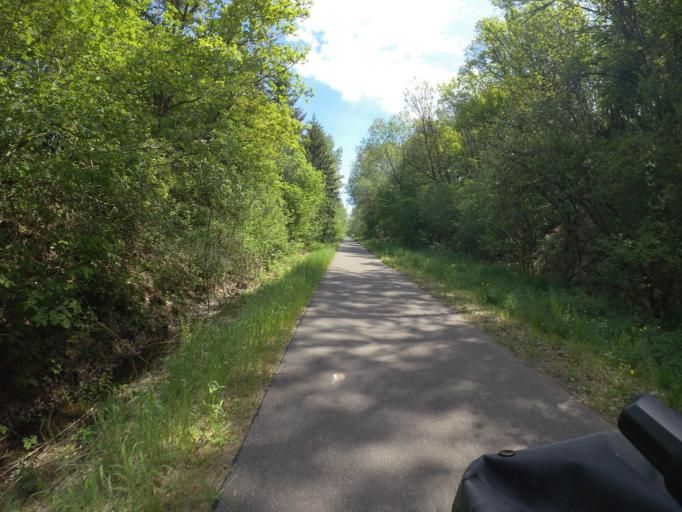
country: DE
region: Rheinland-Pfalz
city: Kerschenbach
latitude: 50.3596
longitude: 6.4831
